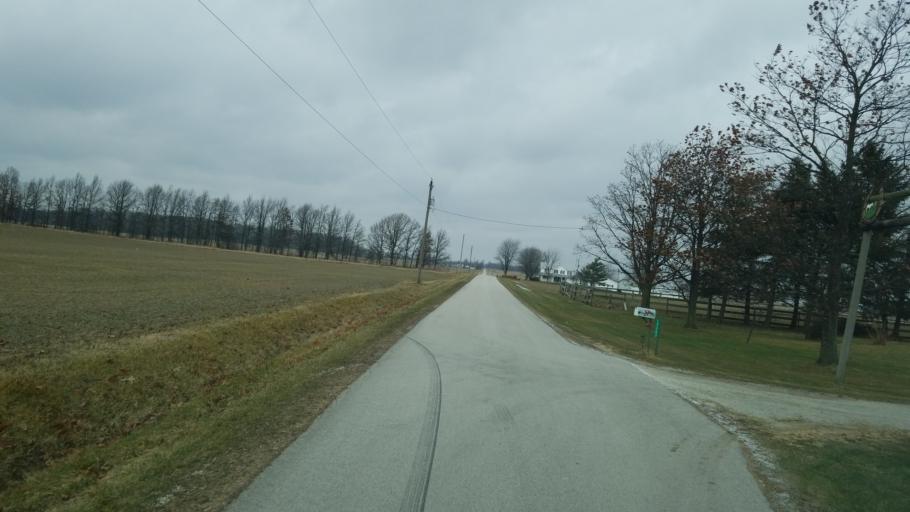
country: US
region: Ohio
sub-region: Hardin County
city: Forest
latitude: 40.7688
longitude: -83.4777
